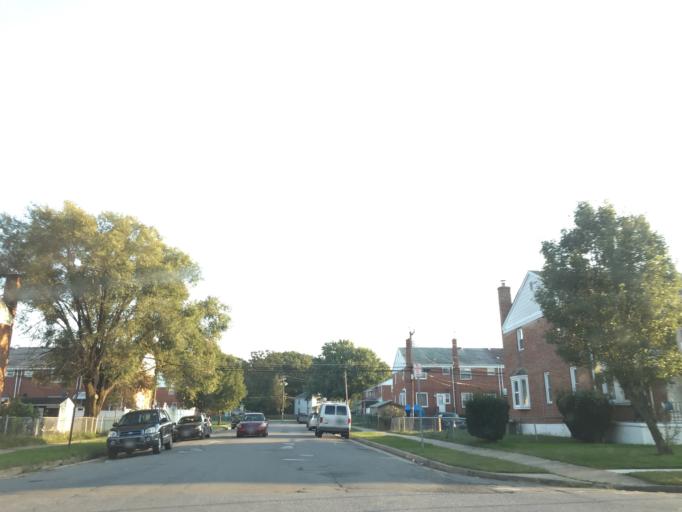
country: US
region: Maryland
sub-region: Baltimore County
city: Middle River
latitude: 39.3269
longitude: -76.4563
